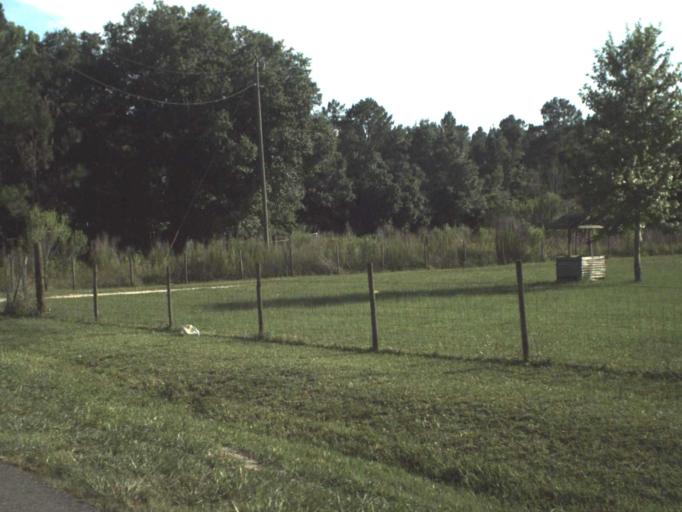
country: US
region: Florida
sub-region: Lake County
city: Clermont
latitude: 28.3840
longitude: -81.8245
